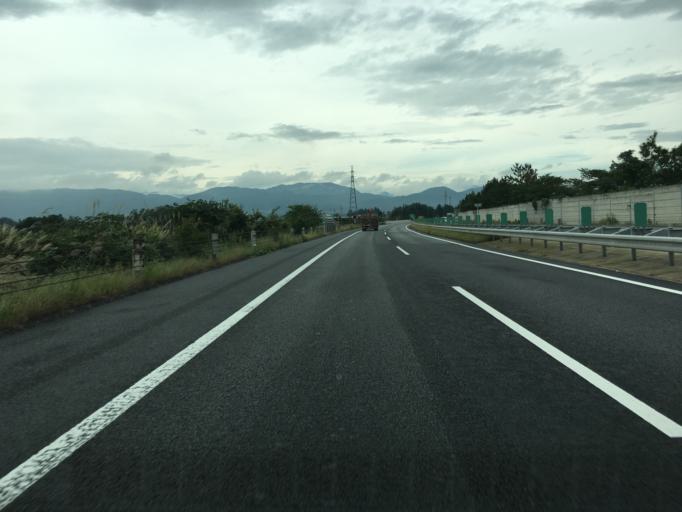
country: JP
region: Fukushima
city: Fukushima-shi
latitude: 37.7527
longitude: 140.4090
